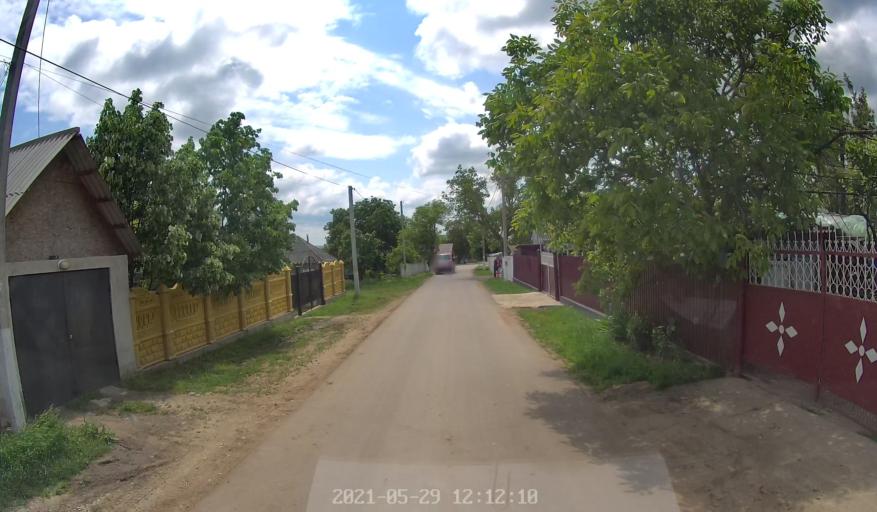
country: MD
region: Hincesti
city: Hincesti
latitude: 46.8802
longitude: 28.6314
